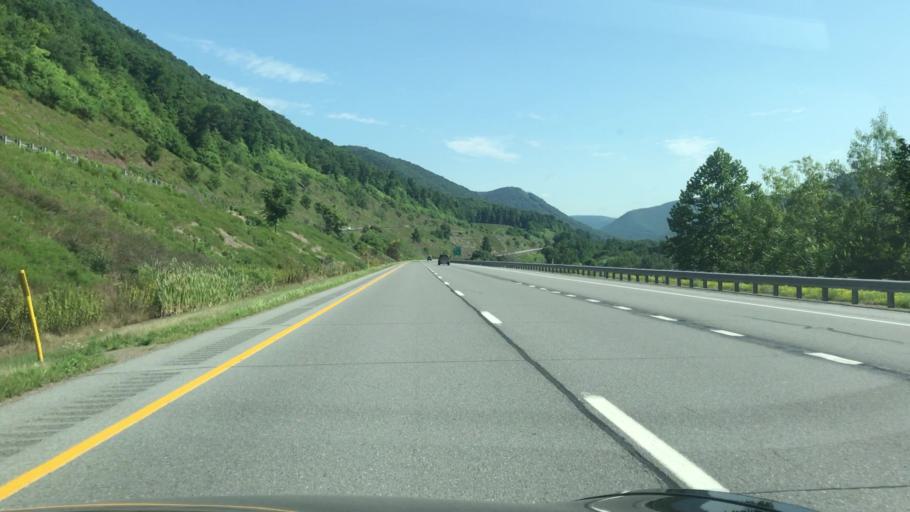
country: US
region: Pennsylvania
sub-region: Lycoming County
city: Garden View
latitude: 41.3578
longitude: -77.0846
